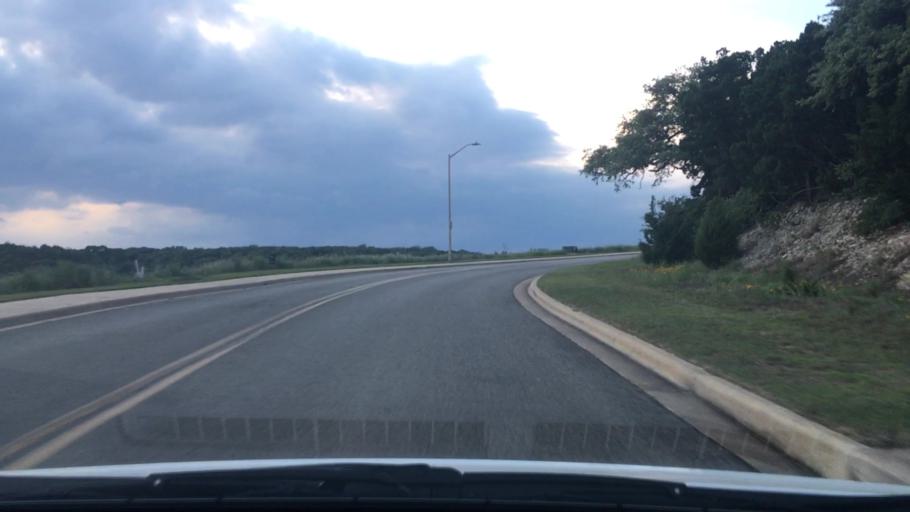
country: US
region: Texas
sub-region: Williamson County
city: Anderson Mill
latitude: 30.4523
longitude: -97.8590
